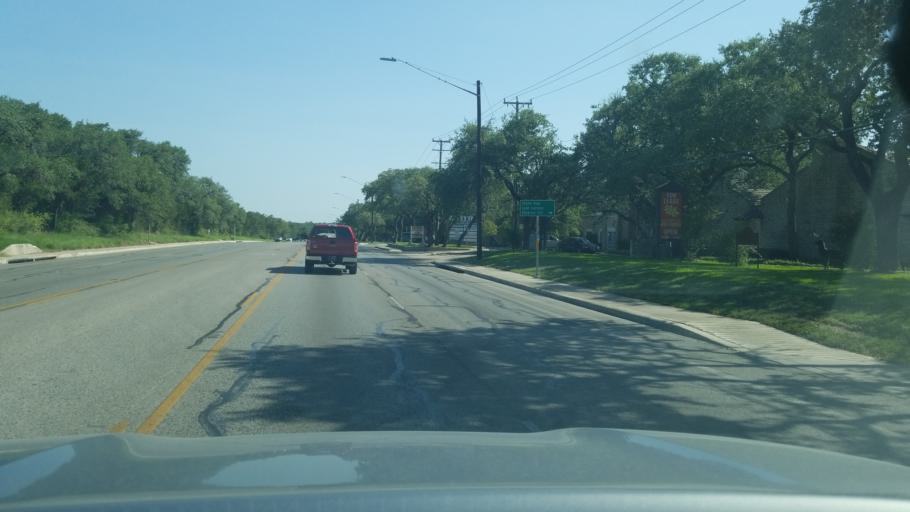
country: US
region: Texas
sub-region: Bexar County
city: Hollywood Park
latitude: 29.5950
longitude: -98.5112
